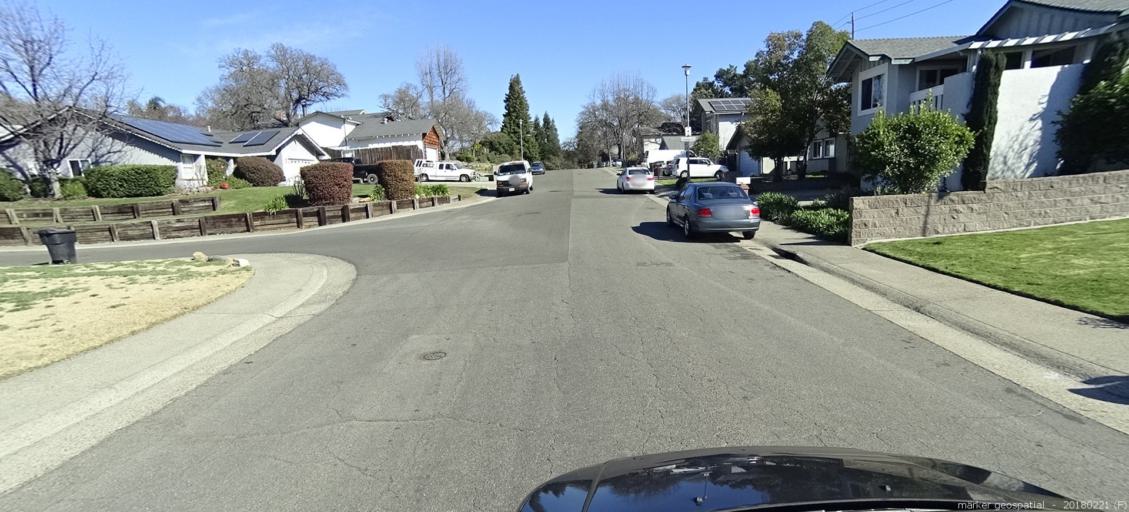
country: US
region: California
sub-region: Sacramento County
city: Citrus Heights
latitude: 38.6863
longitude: -121.2578
